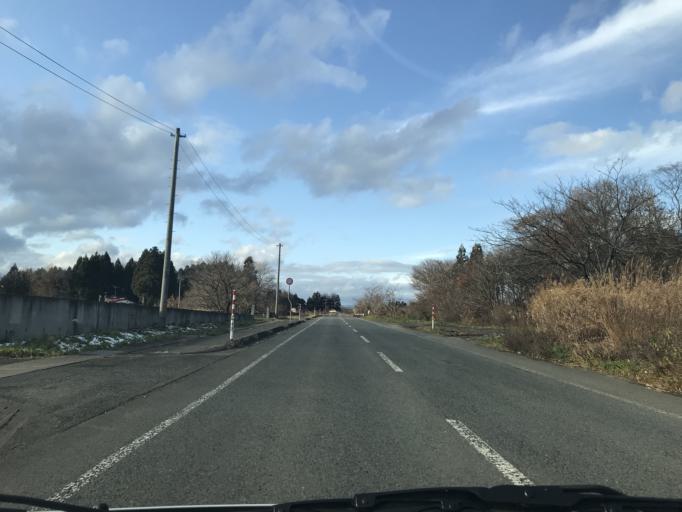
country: JP
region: Iwate
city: Mizusawa
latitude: 39.1932
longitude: 141.0714
